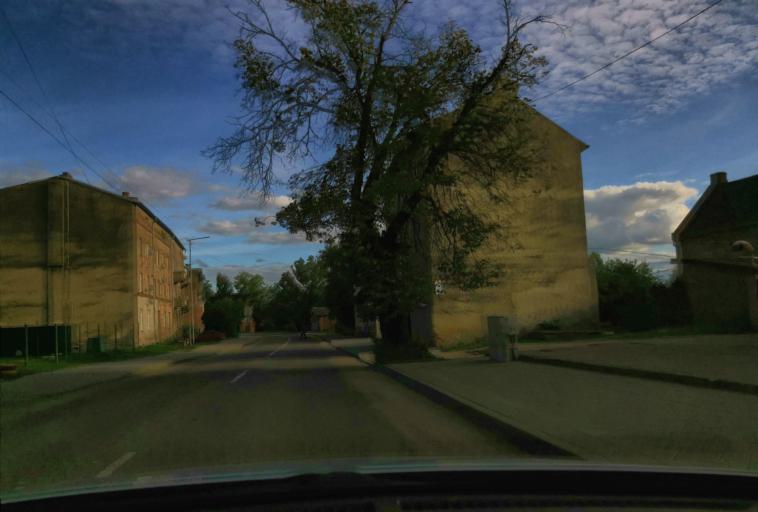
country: RU
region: Kaliningrad
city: Chernyakhovsk
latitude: 54.6266
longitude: 21.8134
